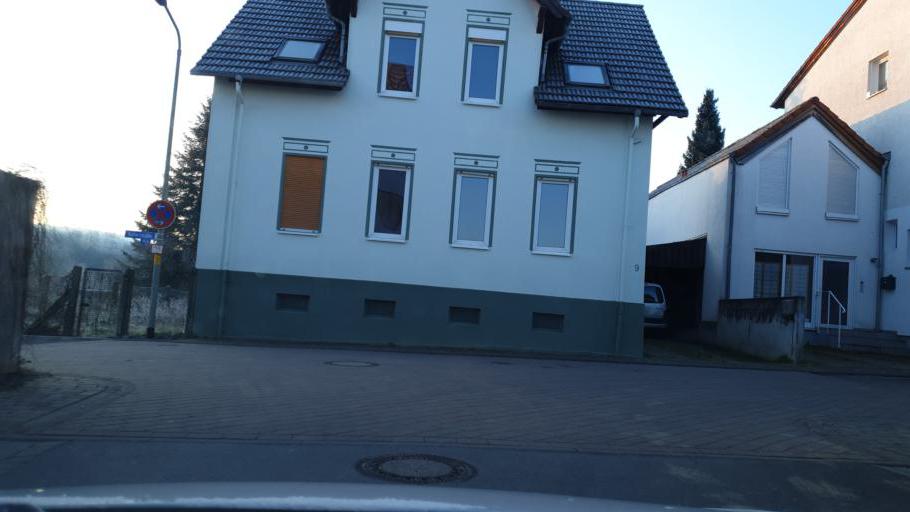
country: DE
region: Hesse
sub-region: Regierungsbezirk Darmstadt
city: Idstein
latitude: 50.2443
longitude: 8.2575
